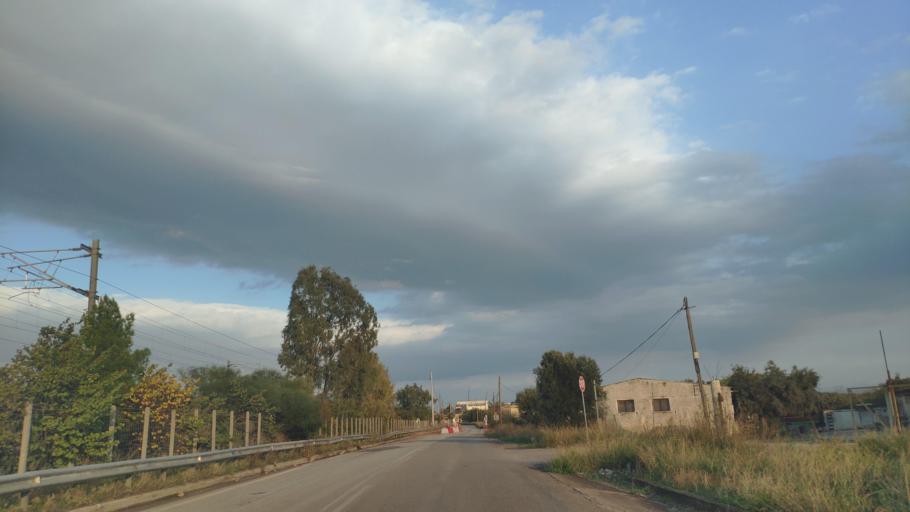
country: GR
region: Attica
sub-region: Nomarchia Dytikis Attikis
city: Nea Peramos
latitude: 38.0052
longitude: 23.3904
